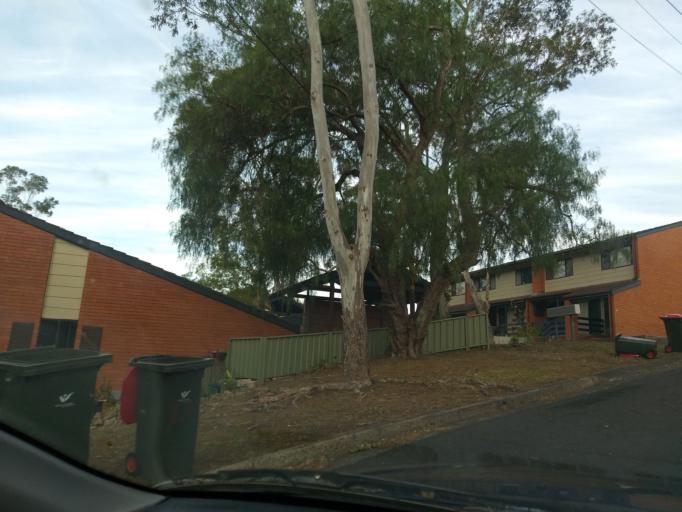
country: AU
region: New South Wales
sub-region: Wollongong
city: Mount Ousley
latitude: -34.3818
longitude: 150.8769
